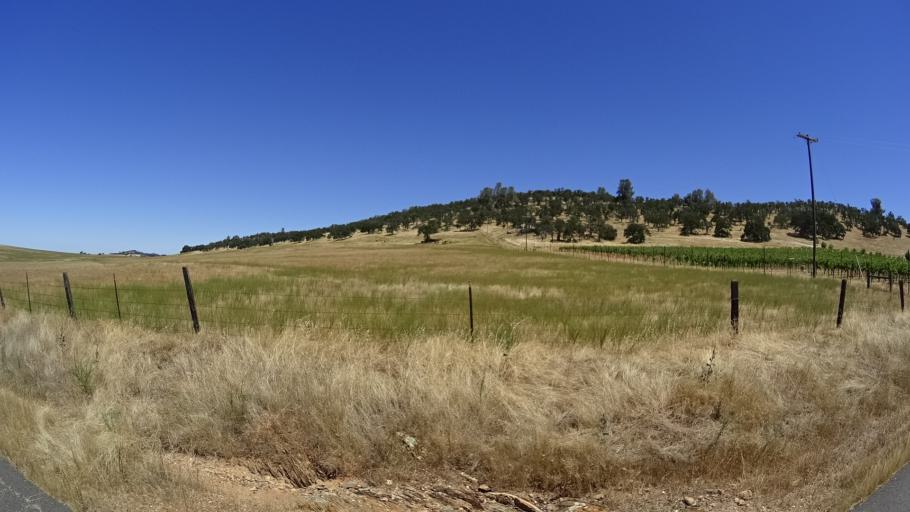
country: US
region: California
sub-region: Calaveras County
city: Copperopolis
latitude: 38.0483
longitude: -120.7052
